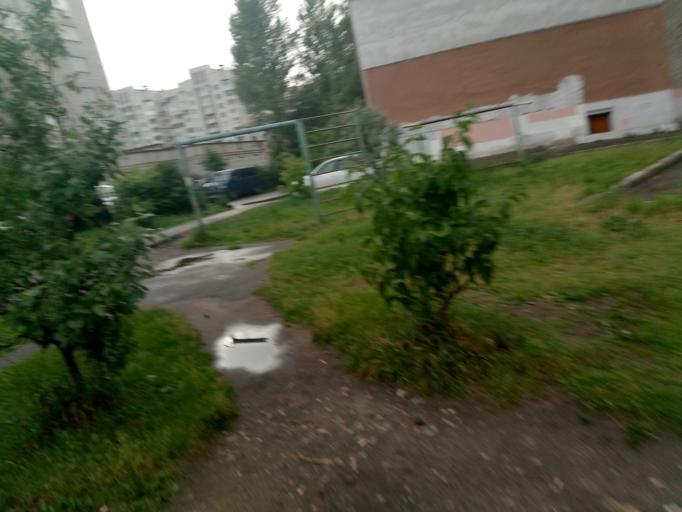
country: RU
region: Jaroslavl
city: Yaroslavl
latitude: 57.6436
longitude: 39.9542
